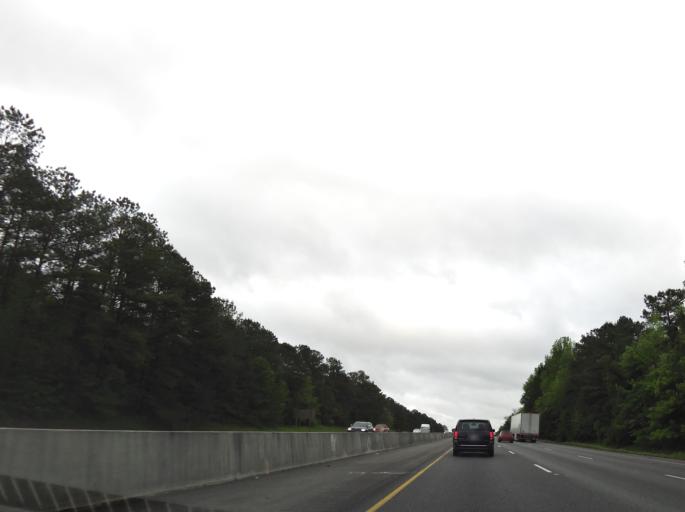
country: US
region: Georgia
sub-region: Bibb County
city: West Point
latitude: 32.9338
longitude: -83.8066
